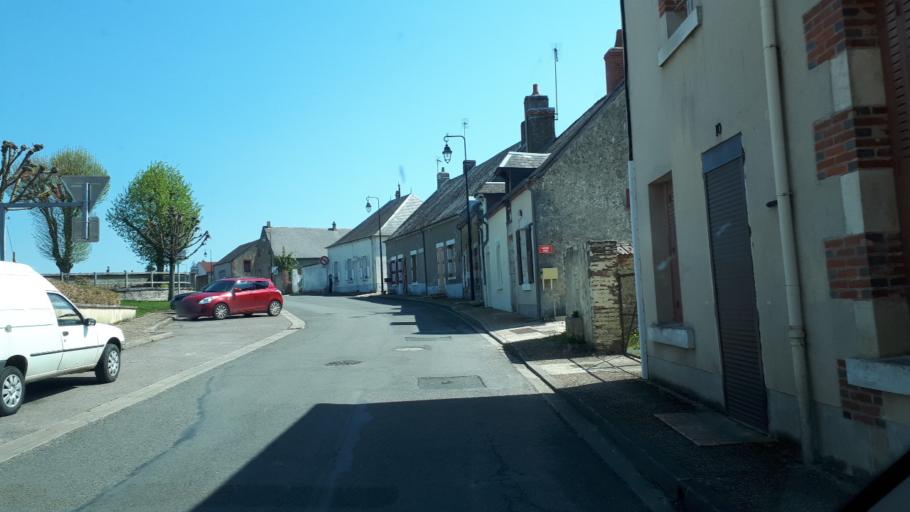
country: FR
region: Centre
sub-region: Departement du Cher
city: Neuvy-sur-Barangeon
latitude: 47.3141
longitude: 2.3631
